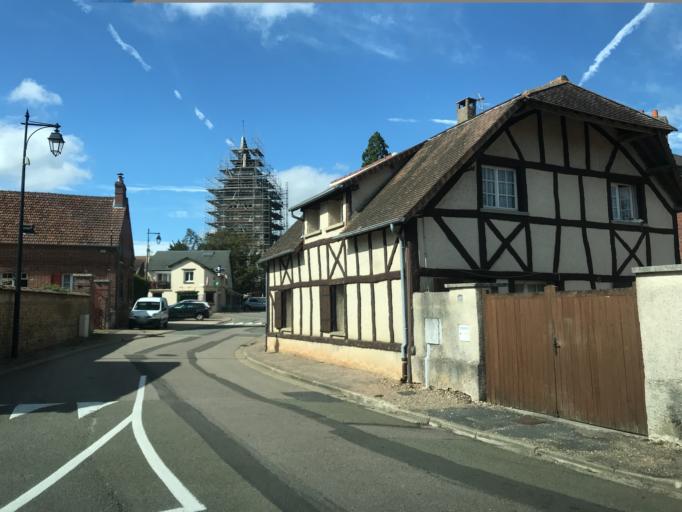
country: FR
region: Haute-Normandie
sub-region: Departement de l'Eure
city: Ande
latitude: 49.1933
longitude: 1.2421
